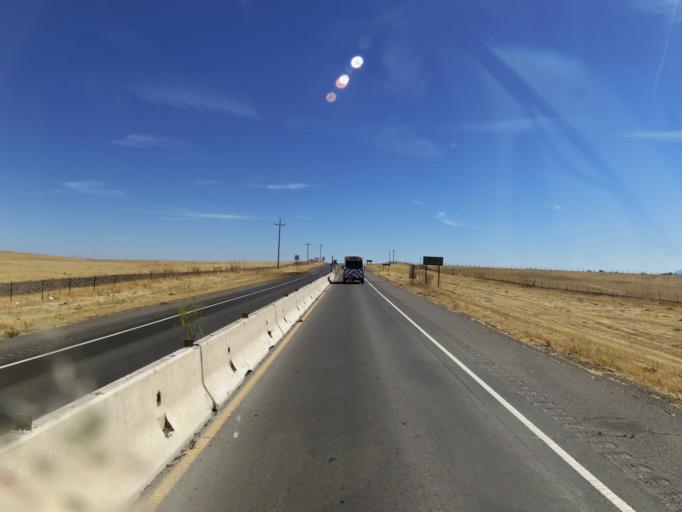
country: US
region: California
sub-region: Solano County
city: Suisun
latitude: 38.2226
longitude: -121.8909
